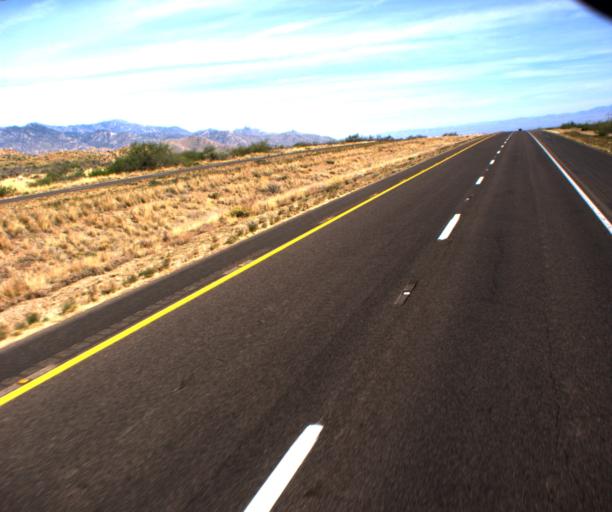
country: US
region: Arizona
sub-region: Graham County
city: Swift Trail Junction
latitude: 32.5288
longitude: -109.6740
